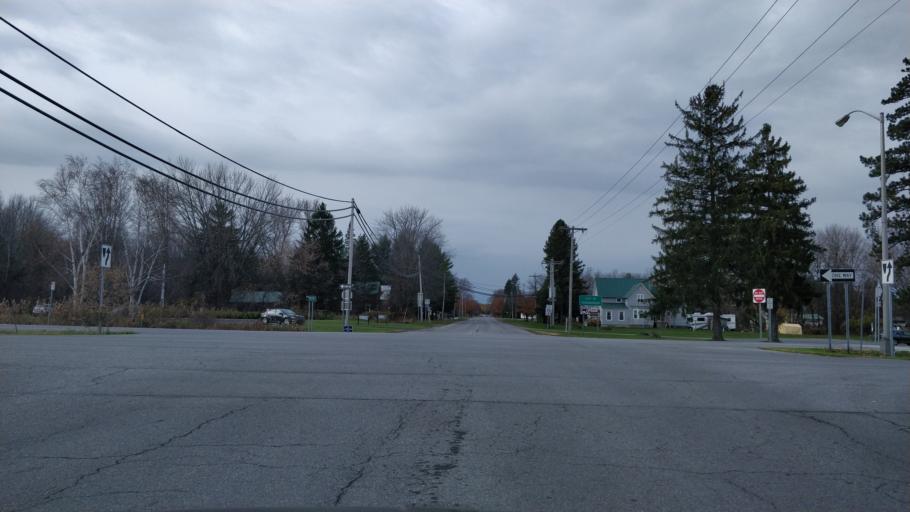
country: US
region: New York
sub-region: St. Lawrence County
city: Ogdensburg
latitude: 44.7156
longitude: -75.4518
